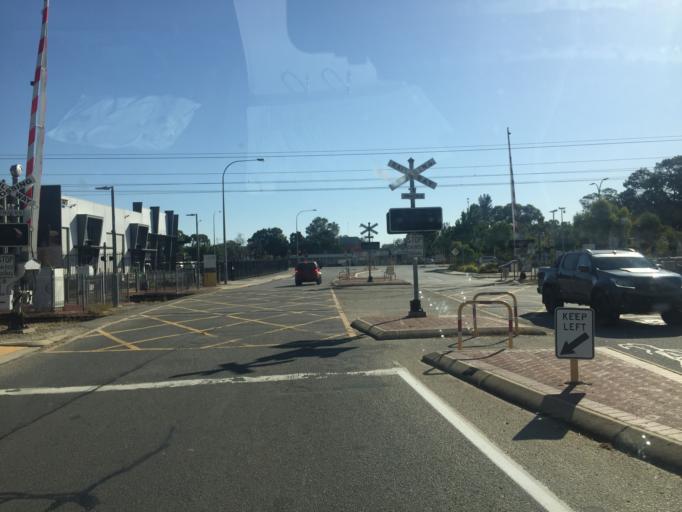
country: AU
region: Western Australia
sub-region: Gosnells
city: Kenwick
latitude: -32.0358
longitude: 115.9695
